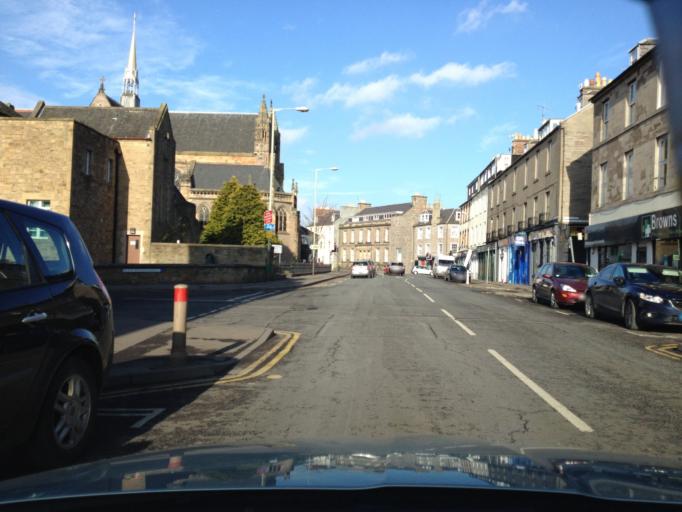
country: GB
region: Scotland
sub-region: Perth and Kinross
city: Perth
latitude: 56.3985
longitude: -3.4347
